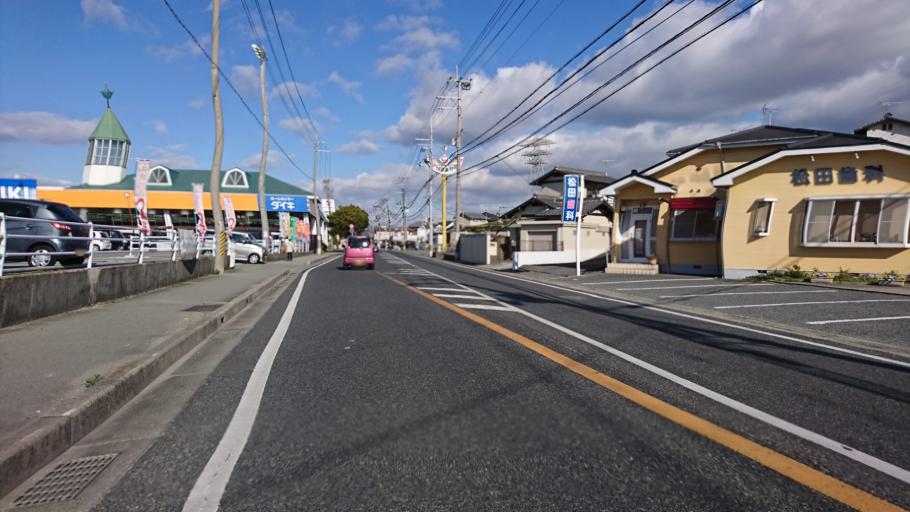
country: JP
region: Hyogo
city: Kakogawacho-honmachi
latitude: 34.7667
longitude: 134.8756
